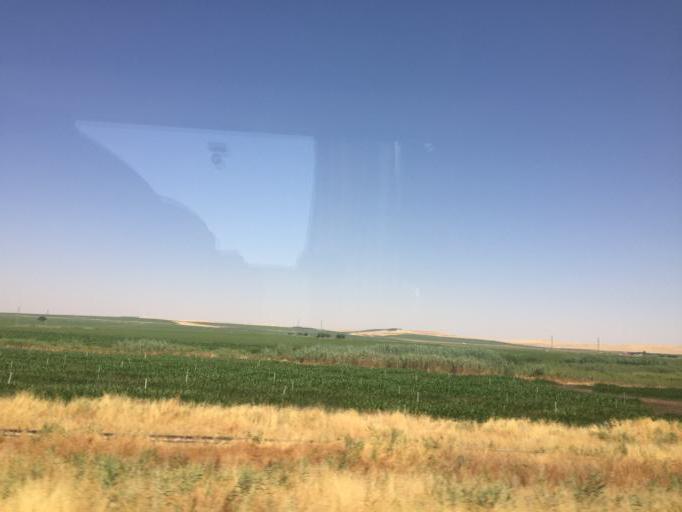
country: TR
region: Diyarbakir
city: Tepe
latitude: 37.8505
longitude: 40.7712
